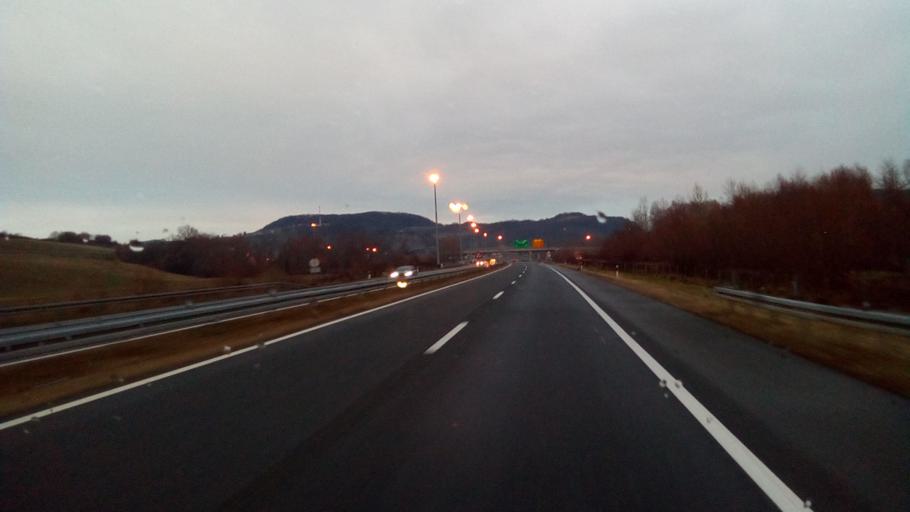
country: HR
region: Varazdinska
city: Remetinec
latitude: 46.0947
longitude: 16.2836
